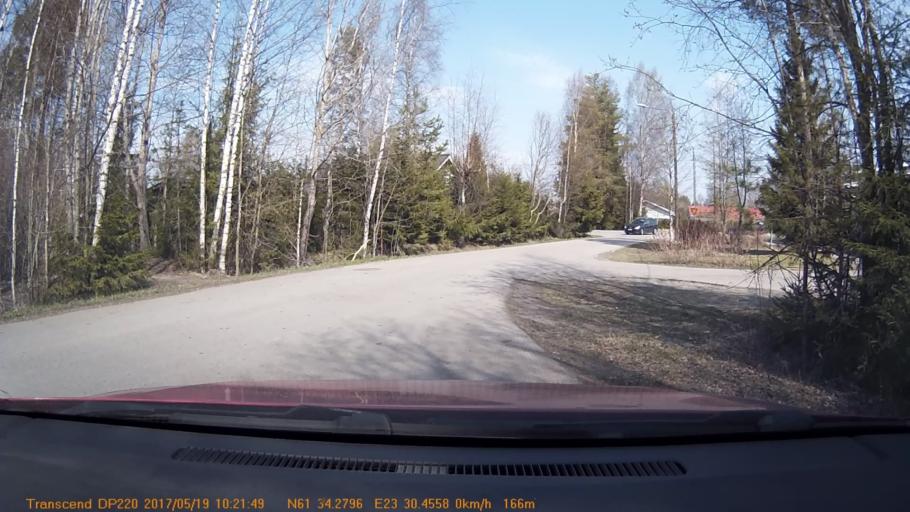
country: FI
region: Pirkanmaa
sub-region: Tampere
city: Yloejaervi
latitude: 61.5713
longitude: 23.5076
